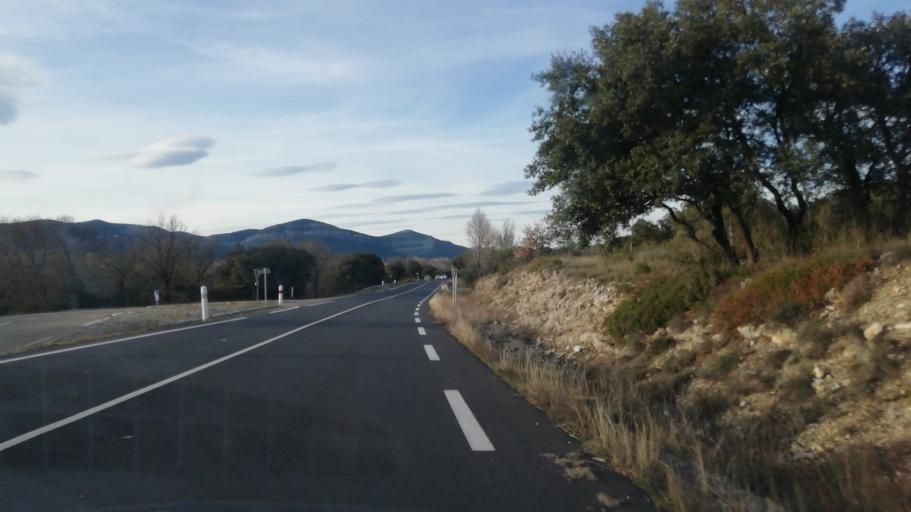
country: FR
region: Languedoc-Roussillon
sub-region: Departement du Gard
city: Quissac
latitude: 43.8866
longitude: 4.0171
